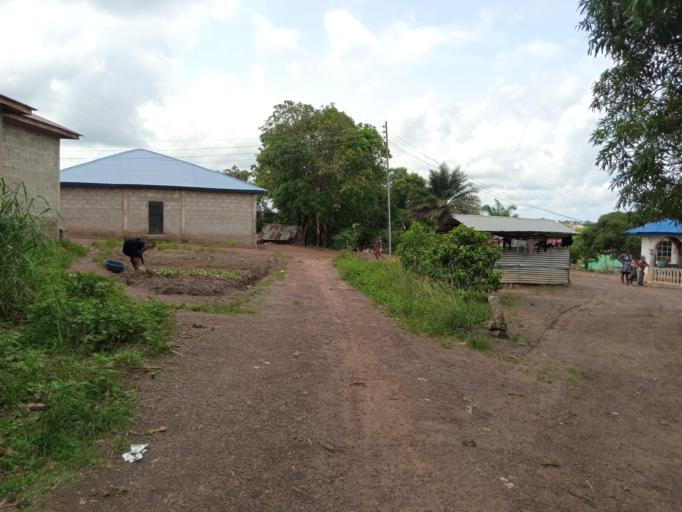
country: SL
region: Southern Province
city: Bo
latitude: 7.9449
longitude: -11.7189
